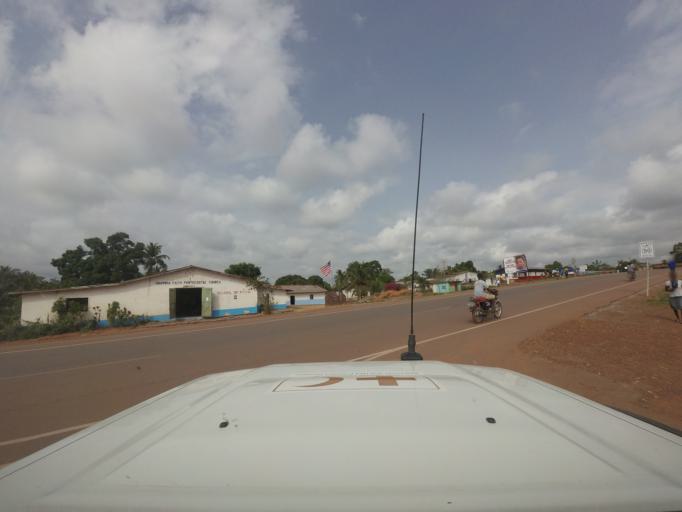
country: LR
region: Bong
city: Gbarnga
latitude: 7.0021
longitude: -9.4754
